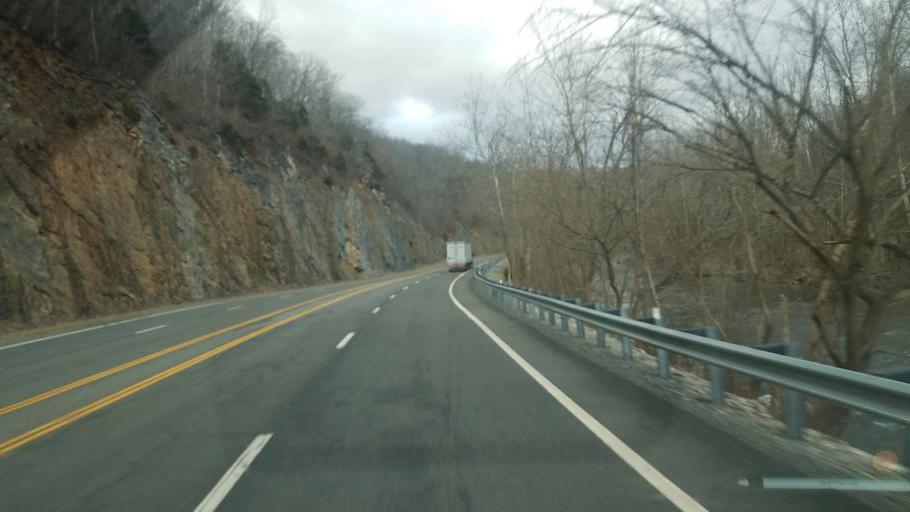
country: US
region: Virginia
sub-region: Giles County
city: Pearisburg
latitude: 37.2554
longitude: -80.7095
